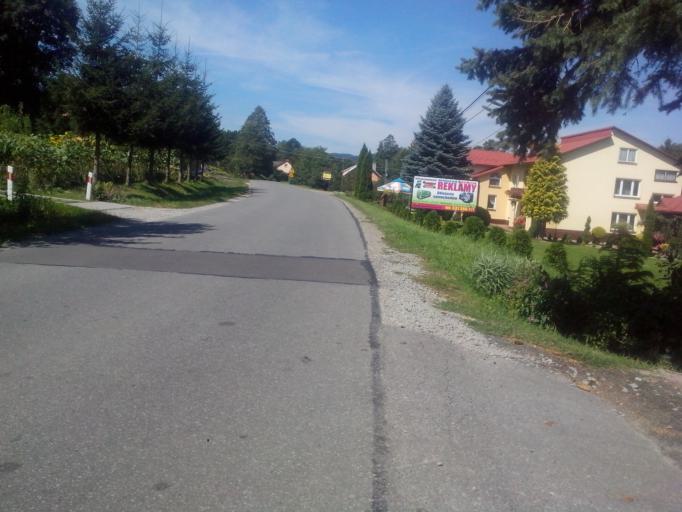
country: PL
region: Subcarpathian Voivodeship
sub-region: Powiat strzyzowski
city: Frysztak
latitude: 49.8673
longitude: 21.6084
